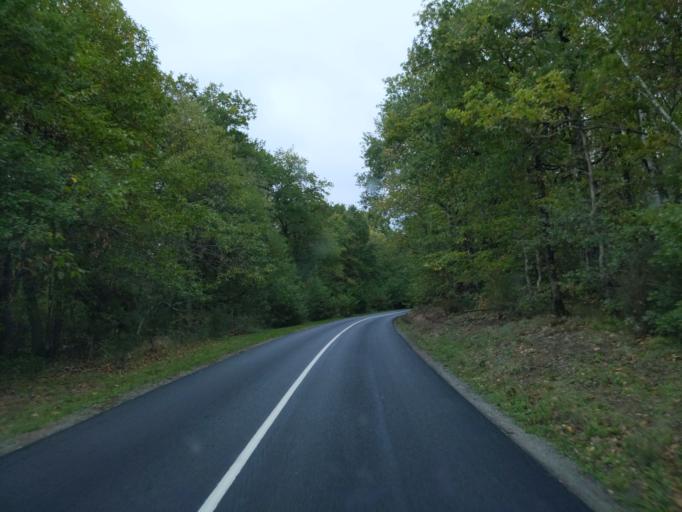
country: FR
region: Ile-de-France
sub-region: Departement des Yvelines
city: Bullion
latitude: 48.6107
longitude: 1.9975
